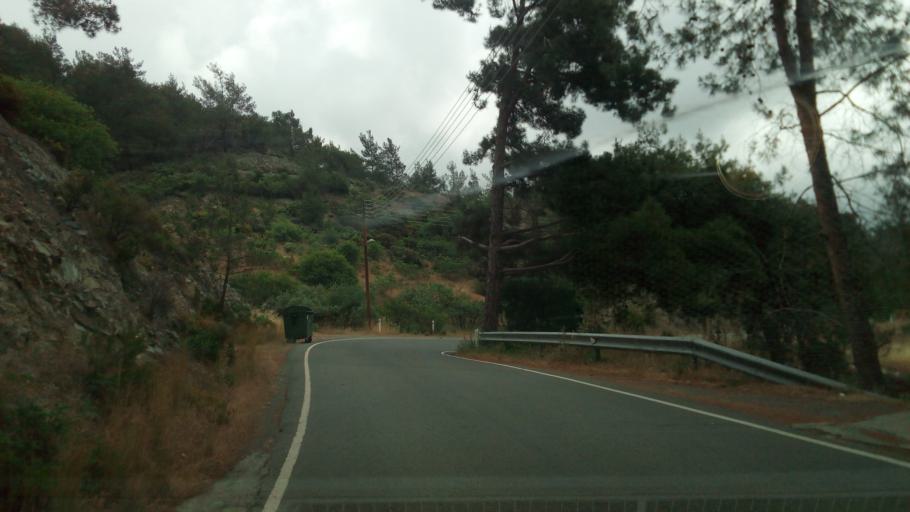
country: CY
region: Limassol
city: Pelendri
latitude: 34.8977
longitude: 32.9944
